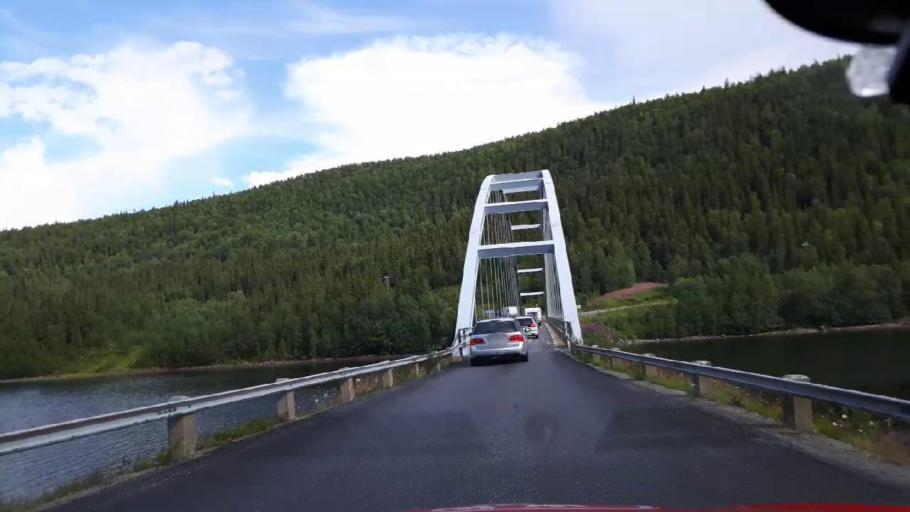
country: SE
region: Vaesterbotten
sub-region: Vilhelmina Kommun
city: Sjoberg
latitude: 65.0311
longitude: 15.1388
